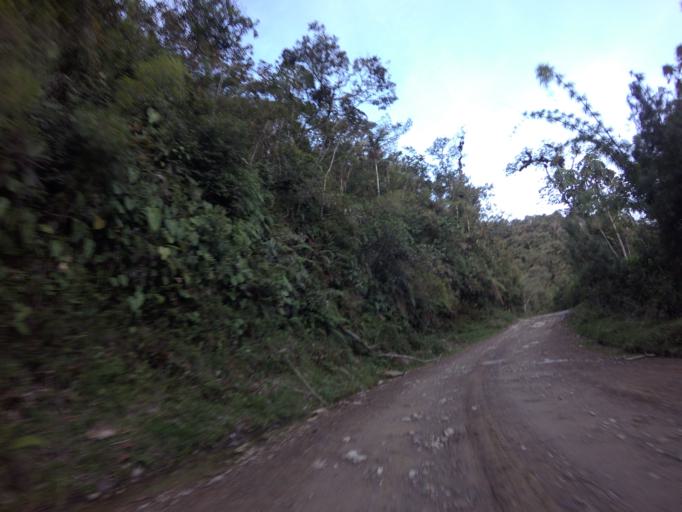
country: CO
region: Caldas
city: Pensilvania
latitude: 5.4593
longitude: -75.1217
